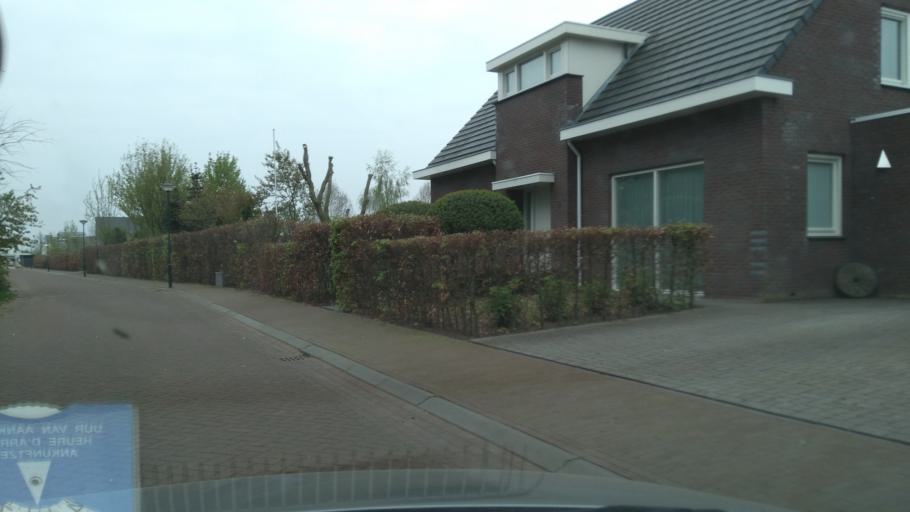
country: NL
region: North Brabant
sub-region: Gemeente Baarle-Nassau
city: Baarle-Nassau
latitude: 51.4798
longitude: 4.9507
